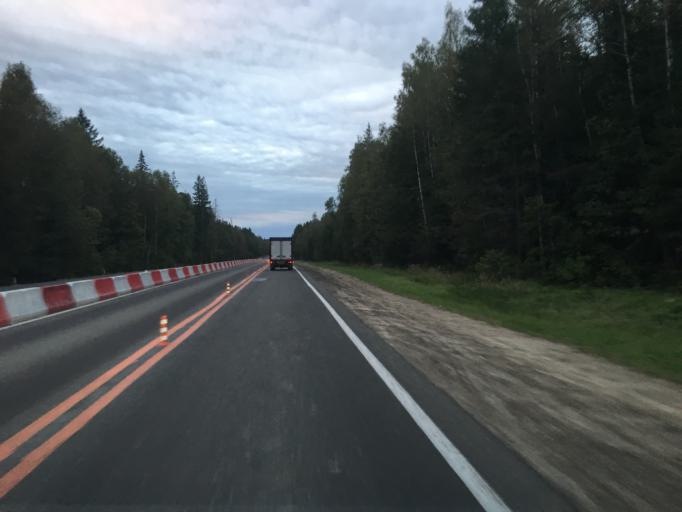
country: RU
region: Kaluga
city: Detchino
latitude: 54.6978
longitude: 36.2941
